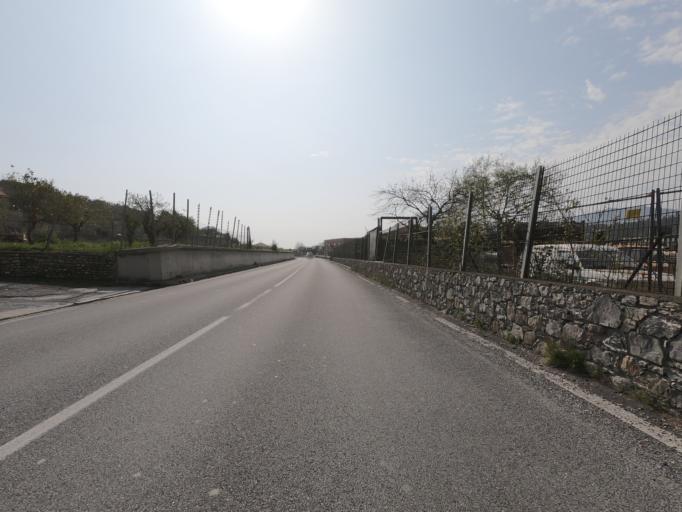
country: IT
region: Liguria
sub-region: Provincia di Savona
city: Cisano
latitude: 44.0762
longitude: 8.1587
